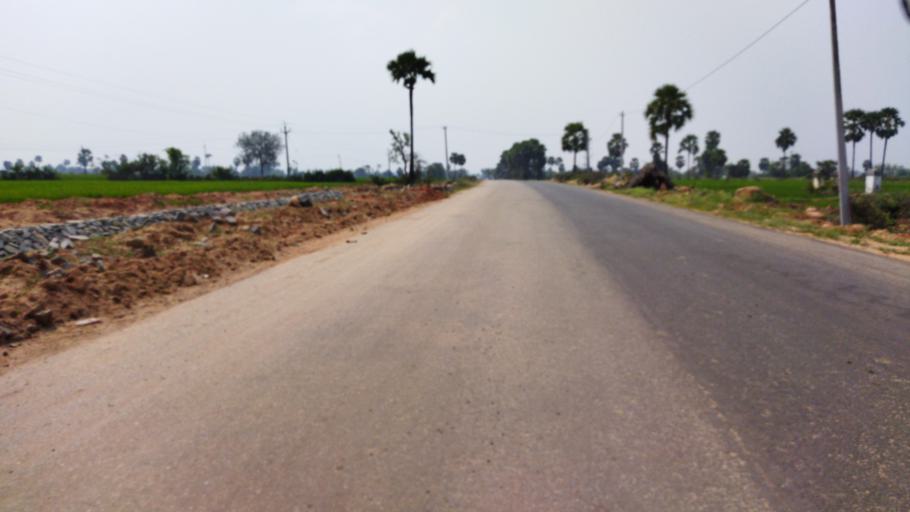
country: IN
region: Telangana
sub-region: Nalgonda
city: Nalgonda
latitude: 17.1107
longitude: 79.3566
